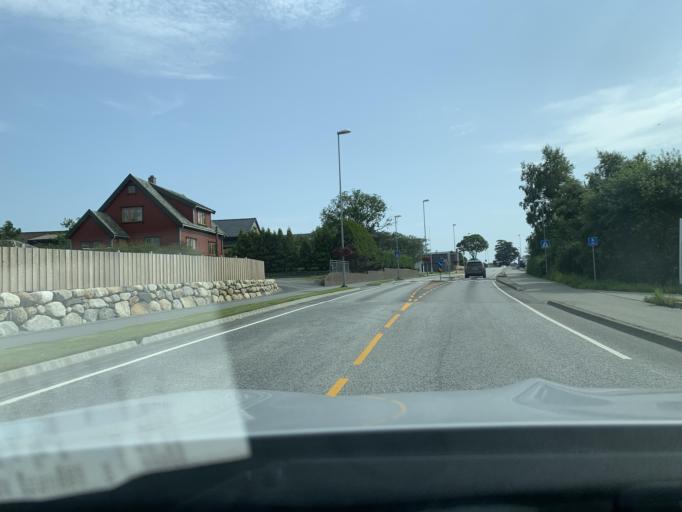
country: NO
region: Rogaland
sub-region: Klepp
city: Kleppe
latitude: 58.7726
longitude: 5.6298
